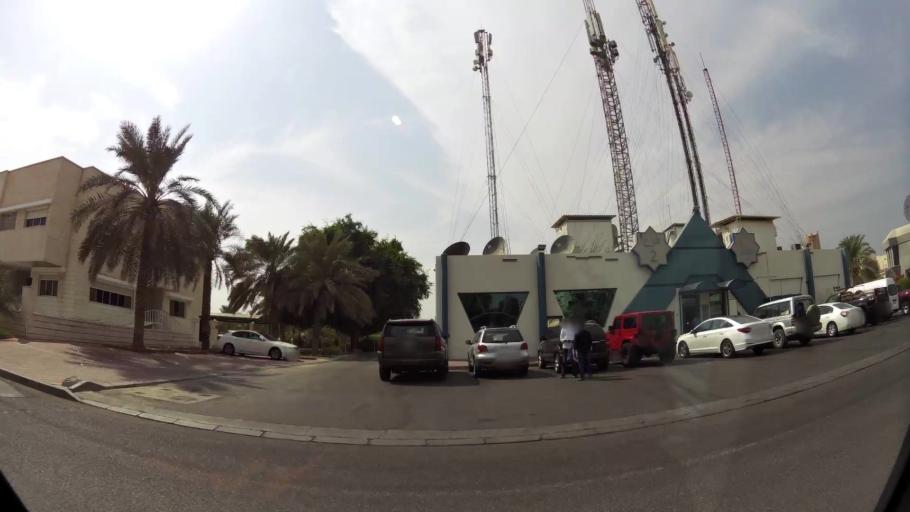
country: KW
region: Al Asimah
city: Ad Dasmah
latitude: 29.3537
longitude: 47.9893
